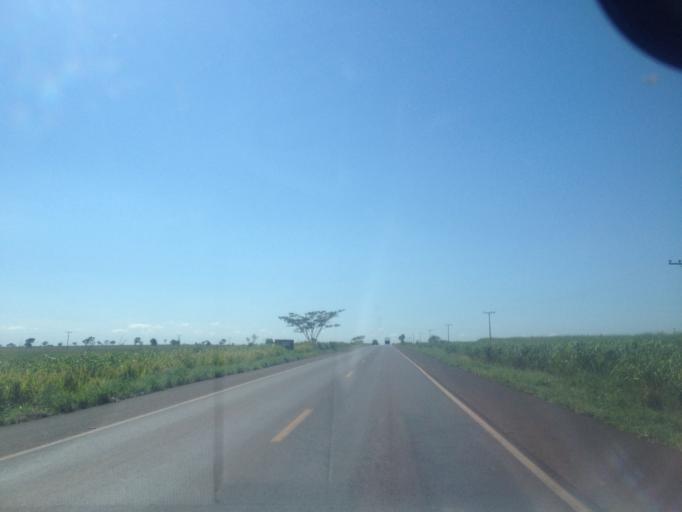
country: BR
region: Minas Gerais
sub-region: Santa Vitoria
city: Santa Vitoria
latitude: -18.9586
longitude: -50.6199
